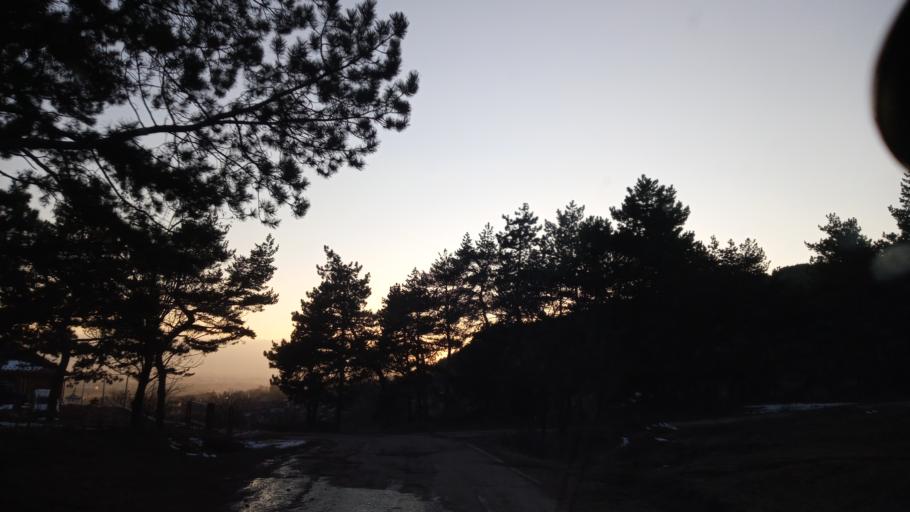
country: BG
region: Sofia-Capital
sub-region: Stolichna Obshtina
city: Bukhovo
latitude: 42.7905
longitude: 23.5226
